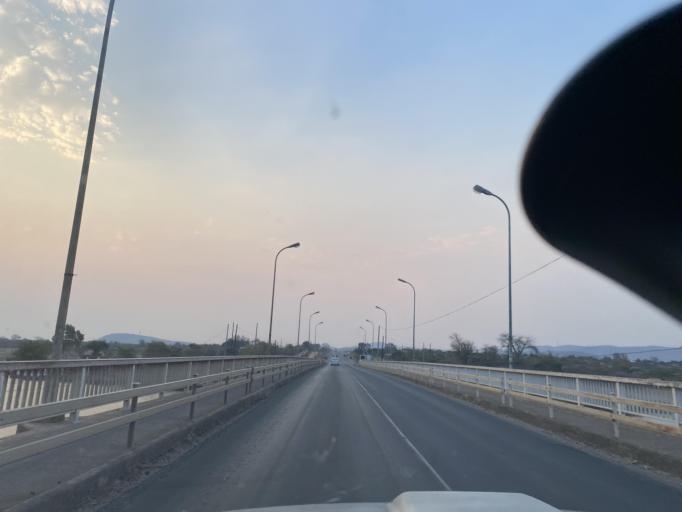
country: ZM
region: Lusaka
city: Kafue
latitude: -15.8380
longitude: 28.2372
